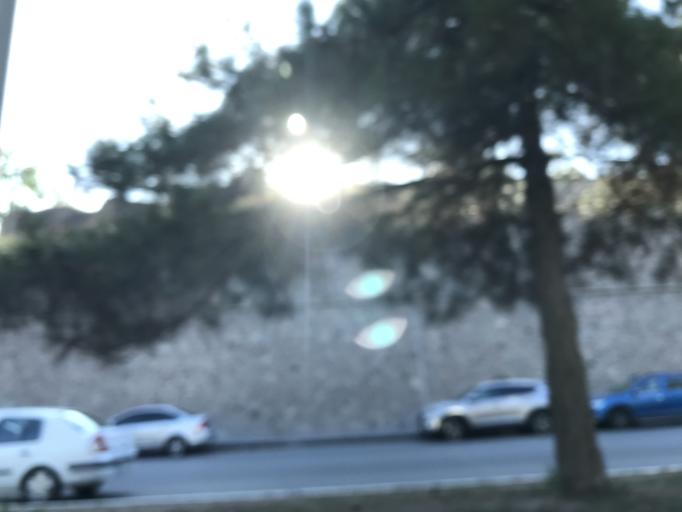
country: TR
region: Ankara
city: Ankara
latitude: 39.9444
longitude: 32.8611
